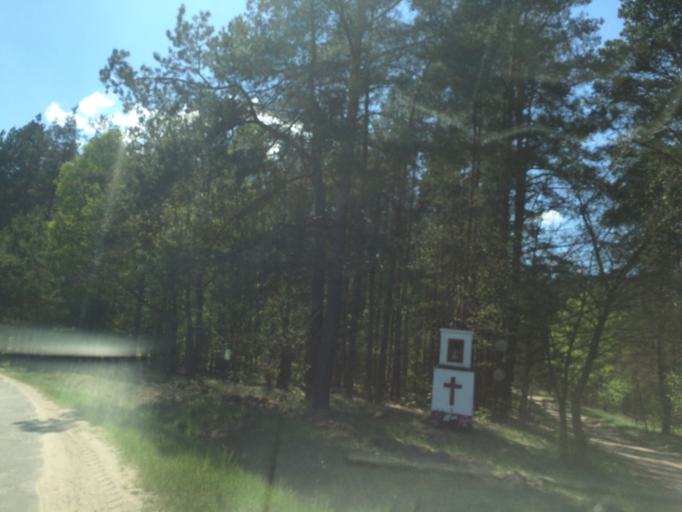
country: PL
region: Warmian-Masurian Voivodeship
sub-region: Powiat nowomiejski
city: Kurzetnik
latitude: 53.3752
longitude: 19.4918
